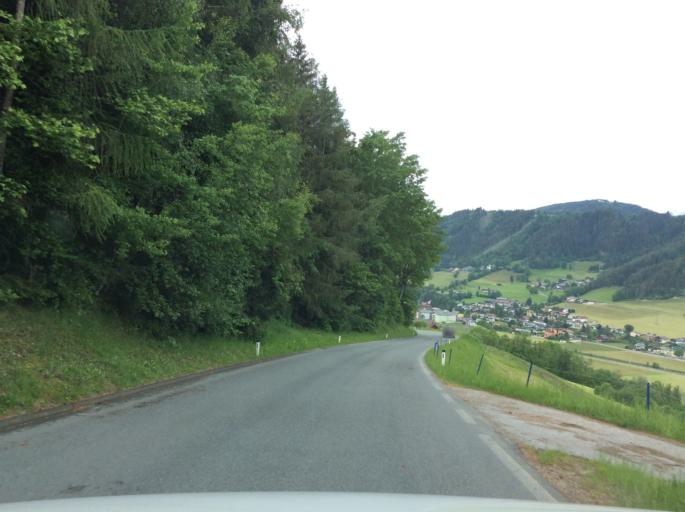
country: AT
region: Styria
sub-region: Politischer Bezirk Liezen
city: Schladming
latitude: 47.3989
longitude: 13.7185
